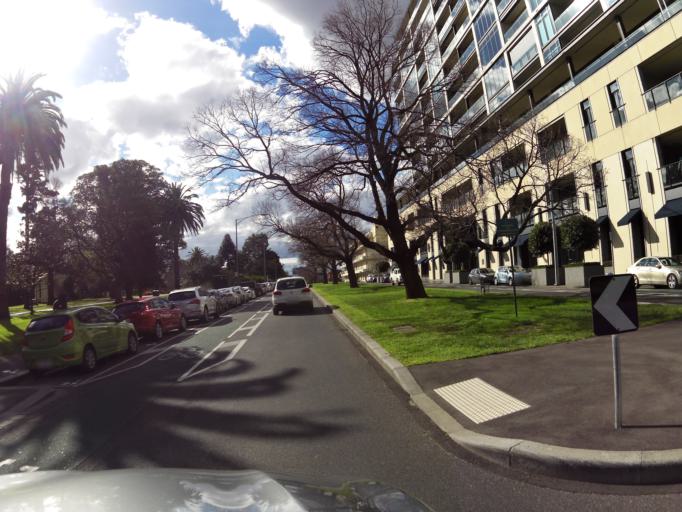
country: AU
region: Victoria
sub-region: Melbourne
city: East Melbourne
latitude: -37.8125
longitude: 144.9831
